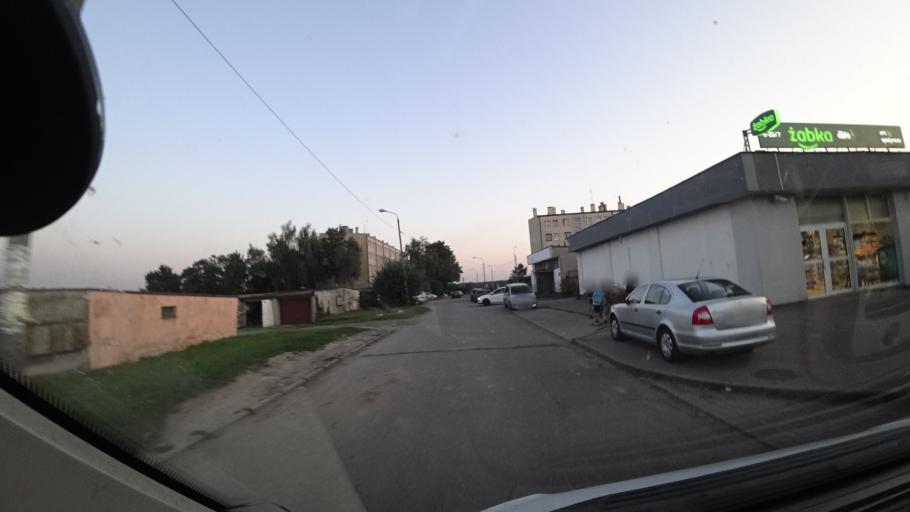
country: PL
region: Silesian Voivodeship
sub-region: Powiat tarnogorski
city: Wieszowa
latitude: 50.3642
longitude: 18.7862
